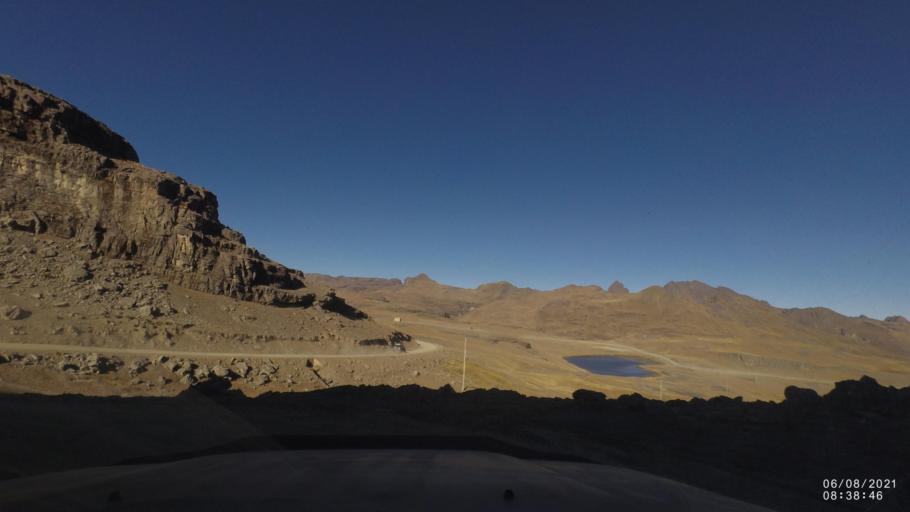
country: BO
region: Cochabamba
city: Sipe Sipe
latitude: -17.1723
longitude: -66.3957
